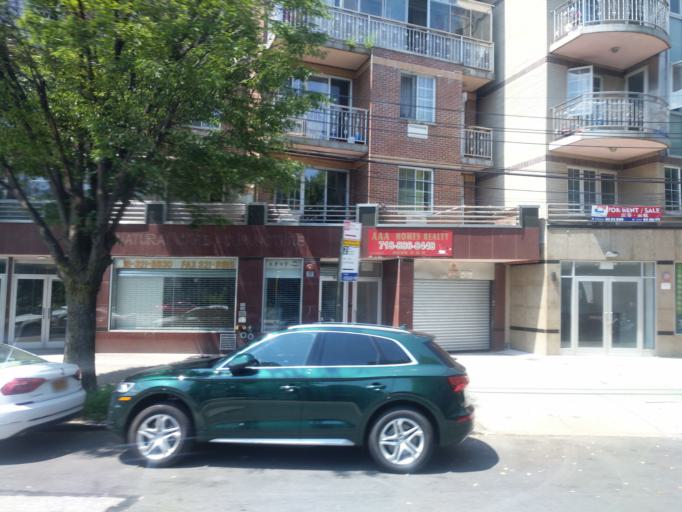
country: US
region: New York
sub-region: Queens County
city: Jamaica
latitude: 40.7693
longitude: -73.8267
